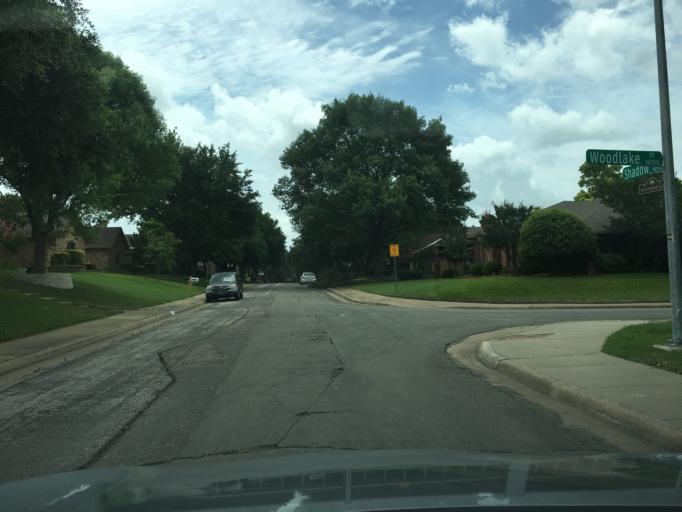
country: US
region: Texas
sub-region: Dallas County
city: Richardson
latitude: 32.9152
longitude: -96.7110
